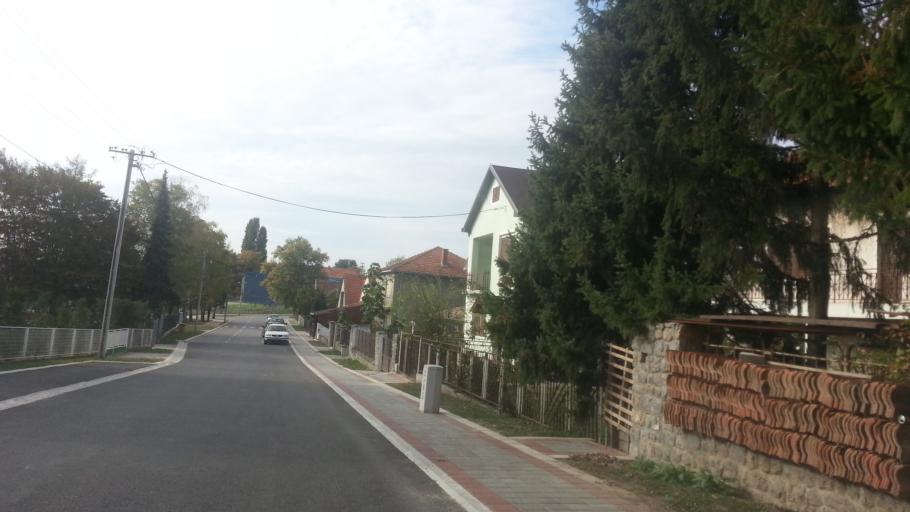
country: RS
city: Belegis
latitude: 45.0172
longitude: 20.3361
